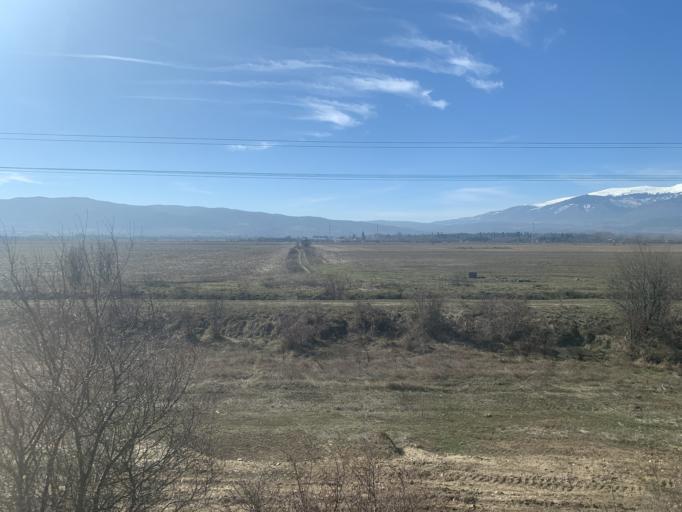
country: BG
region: Sofia-Capital
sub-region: Stolichna Obshtina
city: Sofia
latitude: 42.6572
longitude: 23.4469
